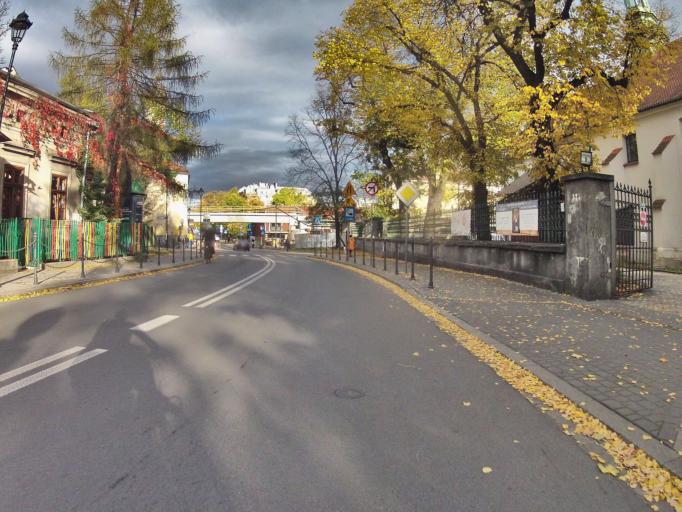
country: PL
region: Lesser Poland Voivodeship
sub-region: Krakow
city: Krakow
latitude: 50.0610
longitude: 19.9466
